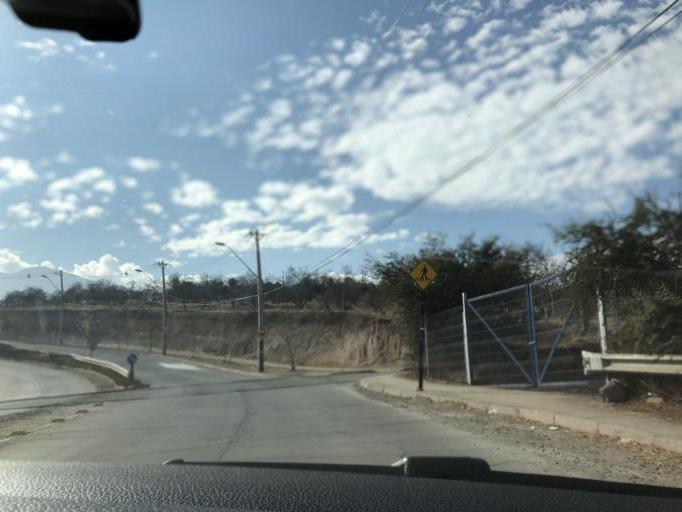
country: CL
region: Santiago Metropolitan
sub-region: Provincia de Cordillera
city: Puente Alto
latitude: -33.5889
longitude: -70.5364
